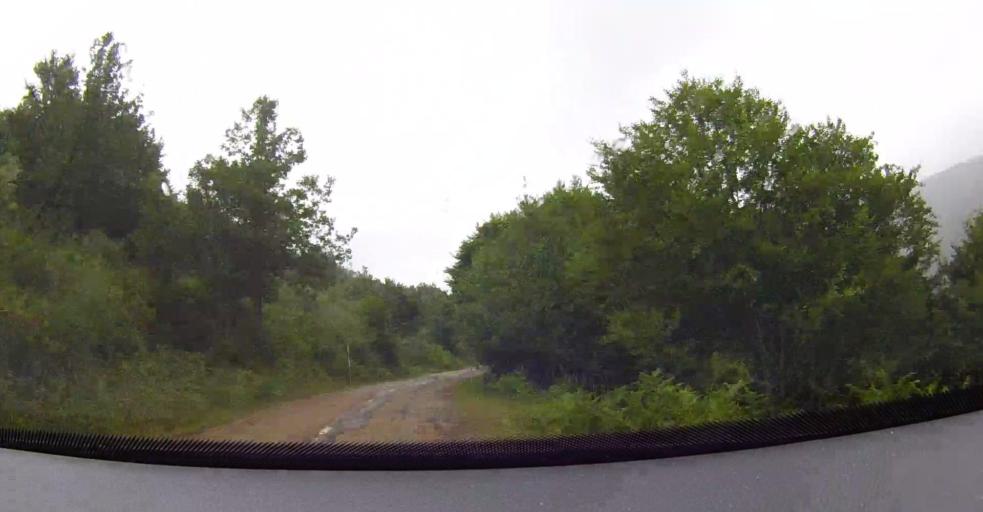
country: ES
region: Castille and Leon
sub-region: Provincia de Leon
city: Puebla de Lillo
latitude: 43.0615
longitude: -5.2739
